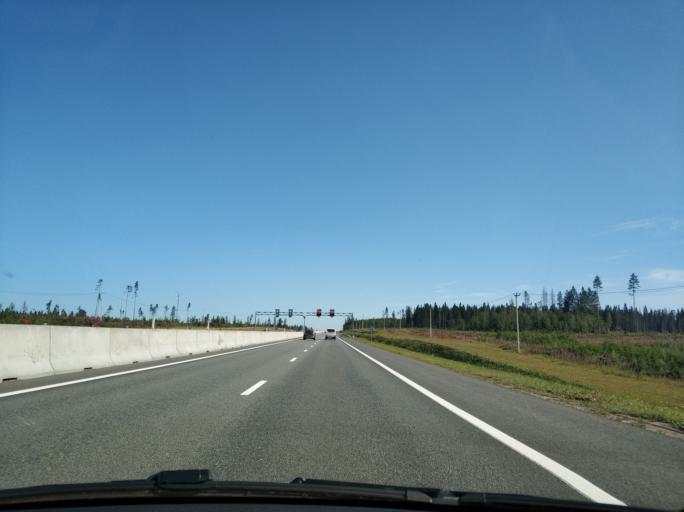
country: RU
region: Leningrad
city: Sosnovo
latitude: 60.4790
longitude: 30.1959
